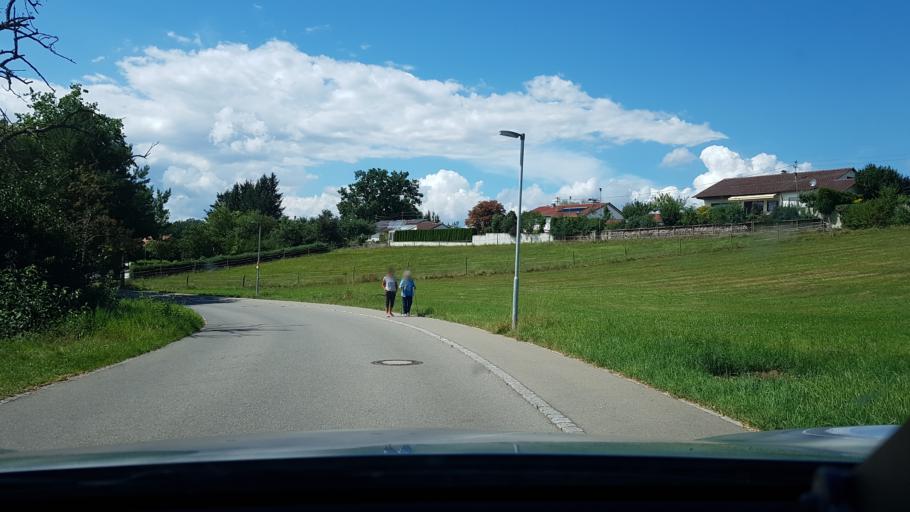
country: DE
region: Baden-Wuerttemberg
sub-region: Tuebingen Region
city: Maselheim
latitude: 48.1550
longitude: 9.8724
